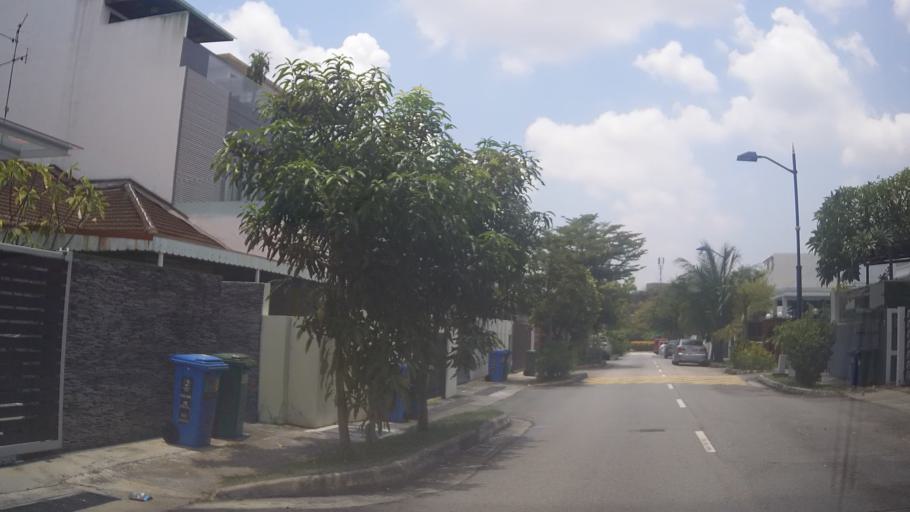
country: SG
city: Singapore
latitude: 1.3666
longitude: 103.8640
